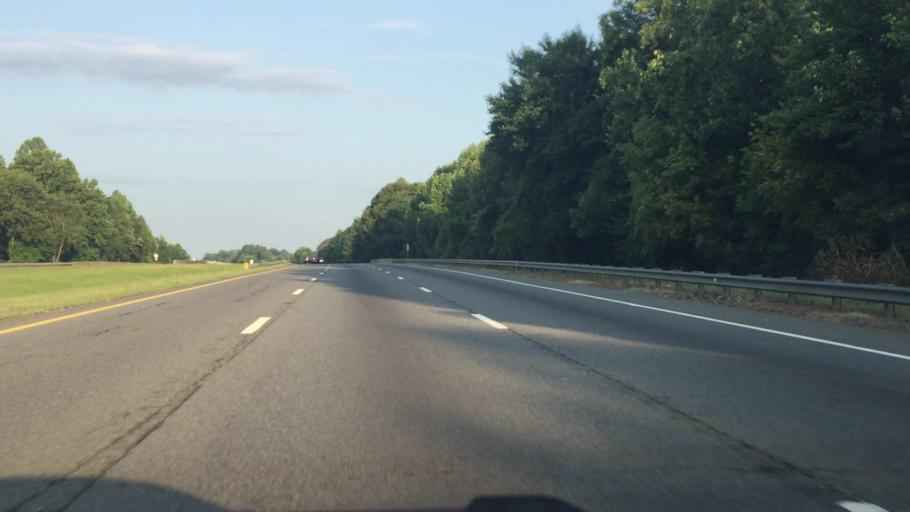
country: US
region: North Carolina
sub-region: Davidson County
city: Lexington
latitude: 35.7770
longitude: -80.2968
